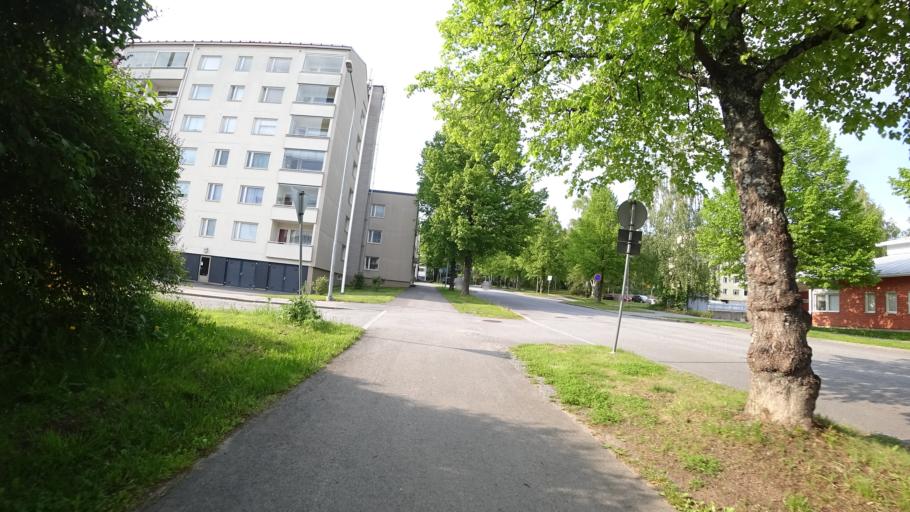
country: FI
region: Pirkanmaa
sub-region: Tampere
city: Pirkkala
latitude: 61.4982
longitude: 23.6383
